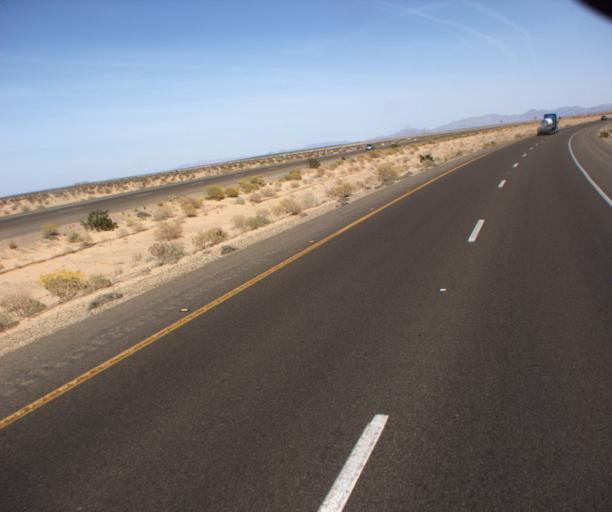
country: US
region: Arizona
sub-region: Yuma County
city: Somerton
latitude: 32.4956
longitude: -114.6572
